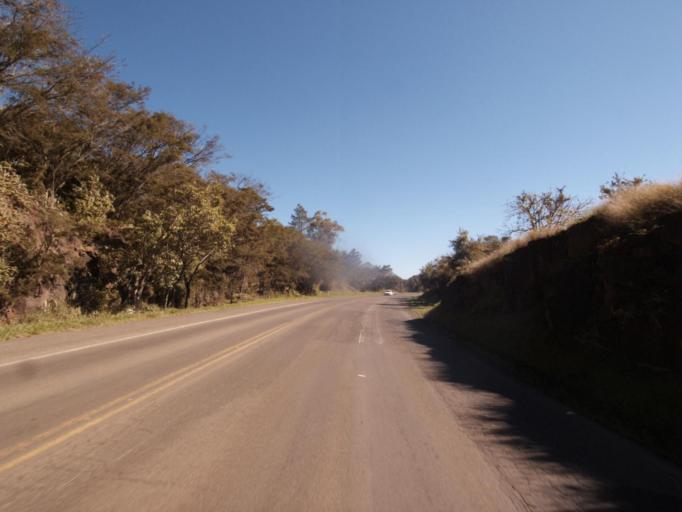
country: AR
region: Misiones
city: Bernardo de Irigoyen
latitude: -26.7661
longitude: -53.4916
